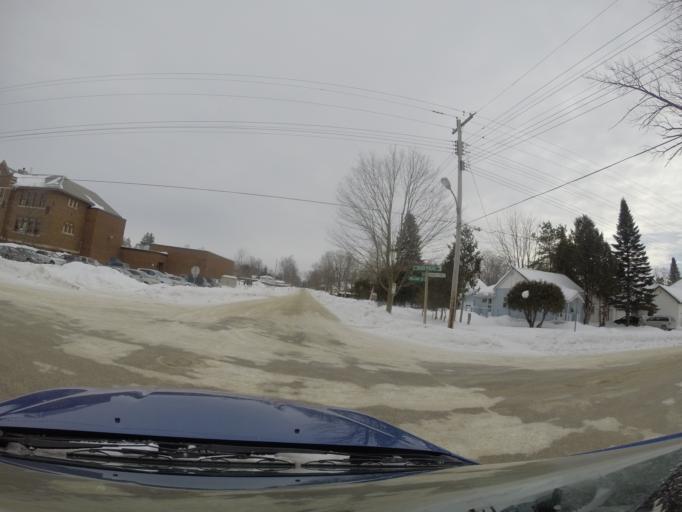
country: CA
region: Ontario
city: Wasaga Beach
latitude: 44.4183
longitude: -80.0912
